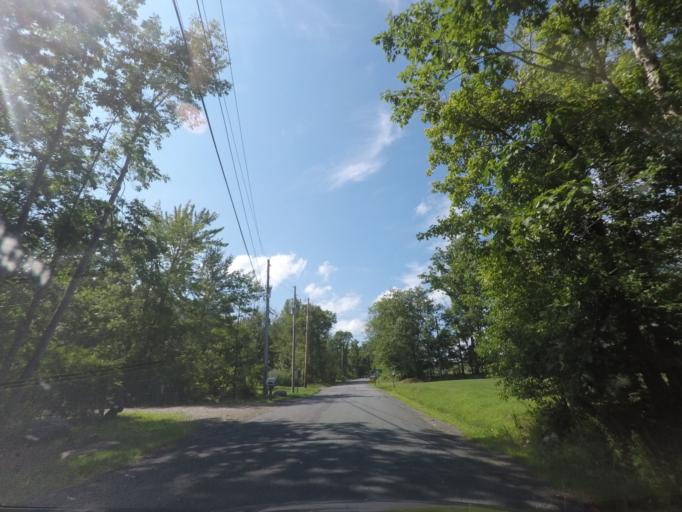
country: US
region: New York
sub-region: Rensselaer County
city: Averill Park
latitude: 42.5958
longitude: -73.5791
